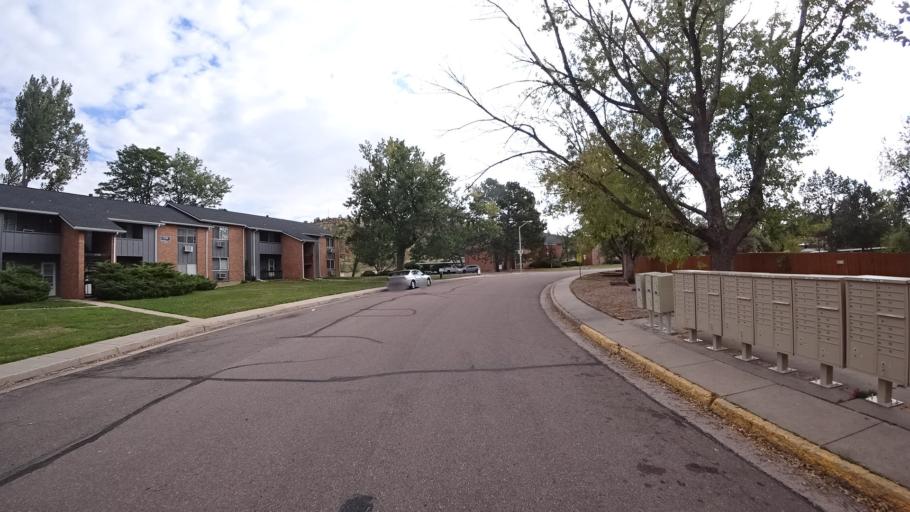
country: US
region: Colorado
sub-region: El Paso County
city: Cimarron Hills
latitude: 38.8576
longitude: -104.7464
